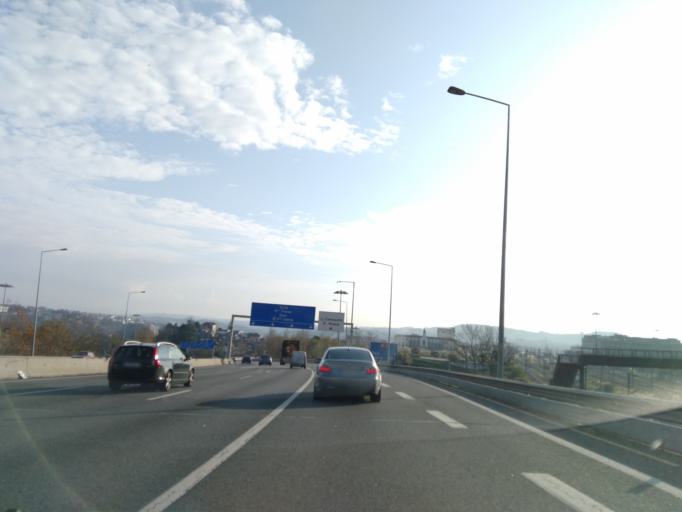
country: PT
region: Porto
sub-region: Porto
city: Porto
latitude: 41.1558
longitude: -8.5832
